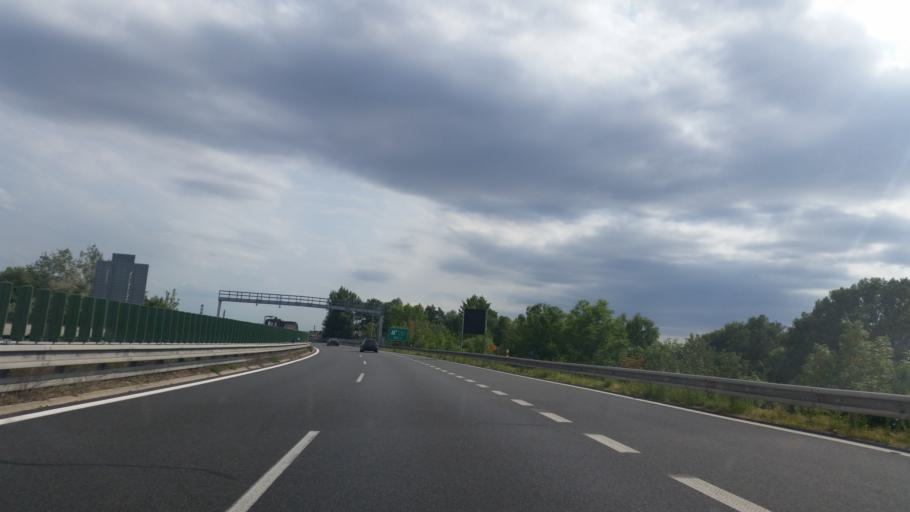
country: CZ
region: Olomoucky
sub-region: Okres Prostejov
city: Prostejov
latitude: 49.4801
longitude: 17.1303
